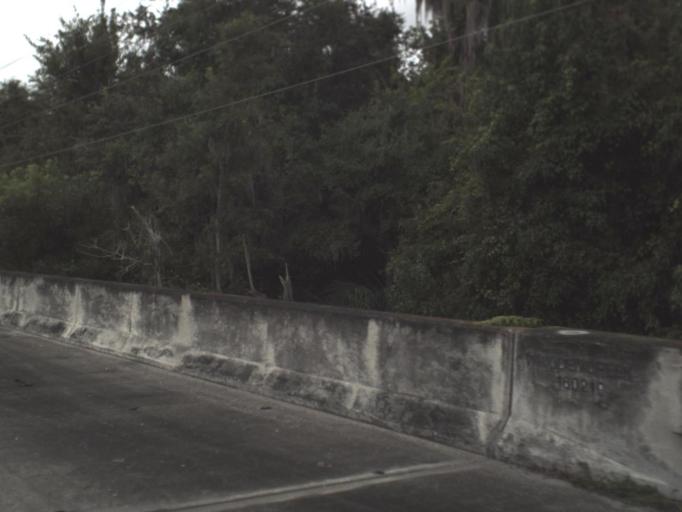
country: US
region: Florida
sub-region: Polk County
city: Fort Meade
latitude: 27.7073
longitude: -81.8074
